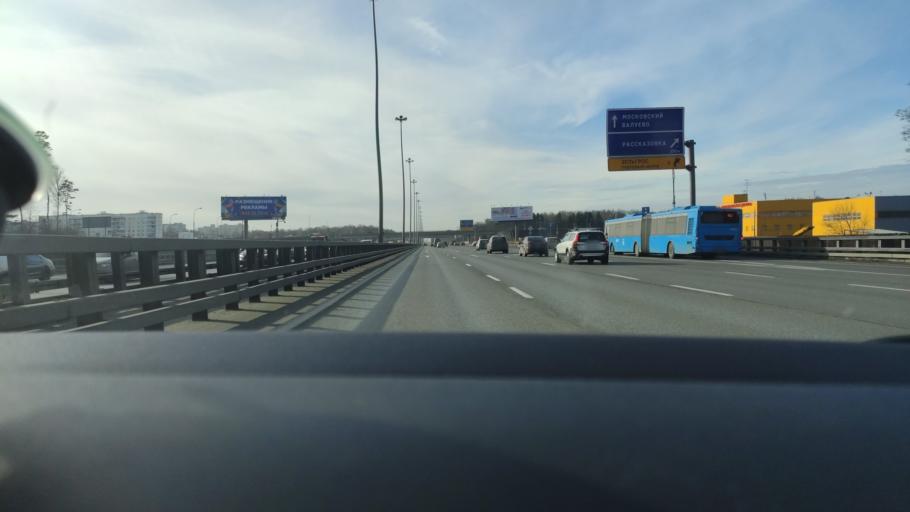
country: RU
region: Moskovskaya
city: Moskovskiy
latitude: 55.6106
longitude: 37.3572
